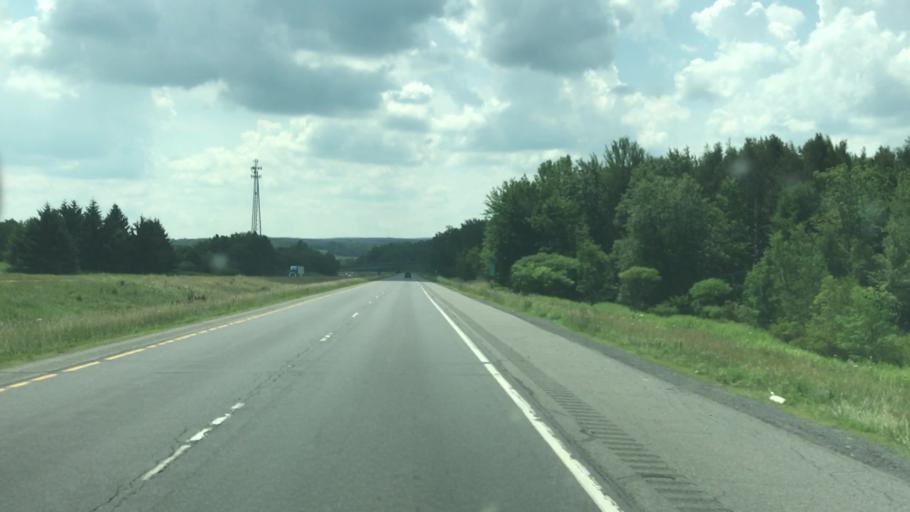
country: US
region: Pennsylvania
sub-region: Lackawanna County
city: Mount Cobb
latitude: 41.3765
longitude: -75.4532
